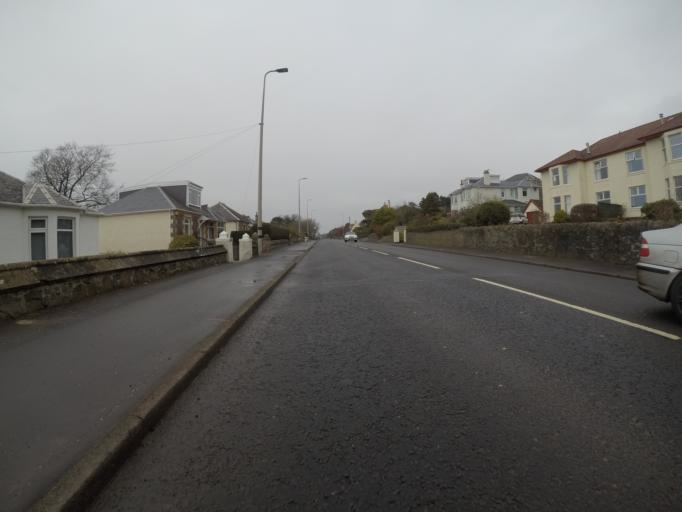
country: GB
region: Scotland
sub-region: North Ayrshire
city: West Kilbride
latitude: 55.6912
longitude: -4.8654
